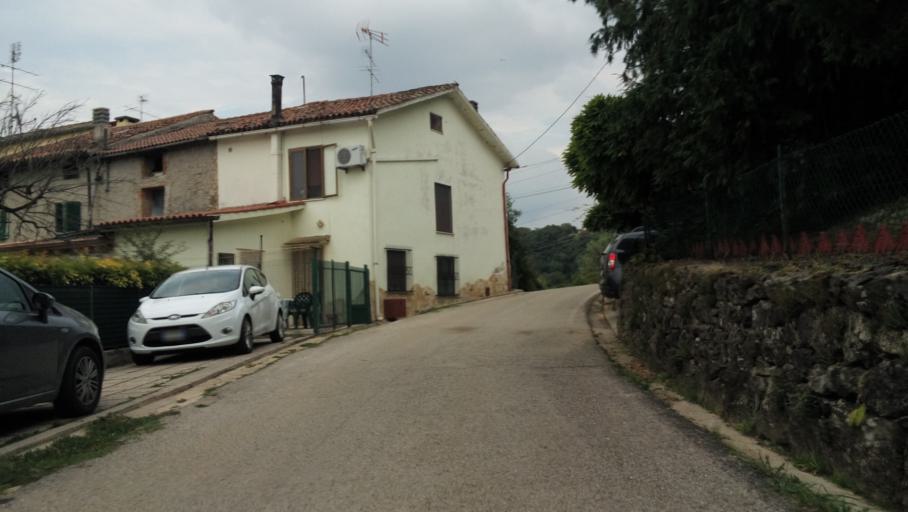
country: IT
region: Veneto
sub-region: Provincia di Vicenza
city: Monteviale
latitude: 45.5520
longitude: 11.4661
